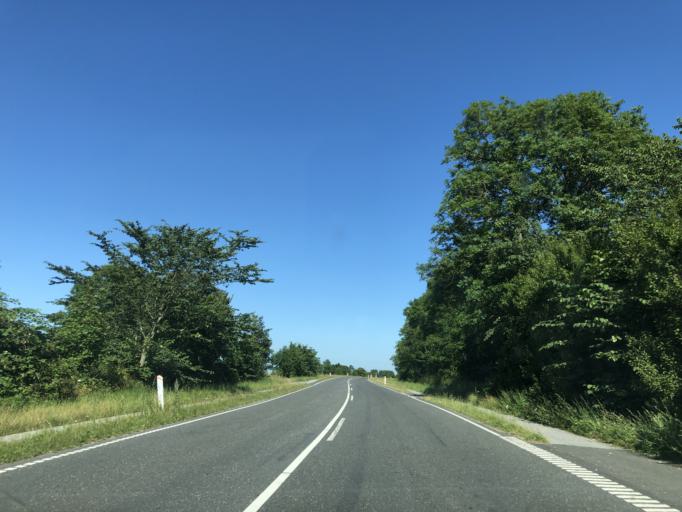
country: DK
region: Central Jutland
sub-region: Syddjurs Kommune
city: Ronde
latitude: 56.2995
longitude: 10.4900
